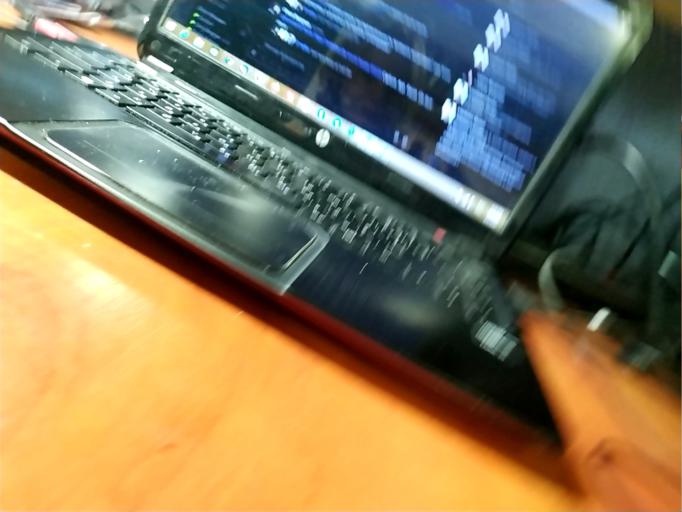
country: RU
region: Tverskaya
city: Sandovo
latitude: 58.5981
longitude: 36.4179
